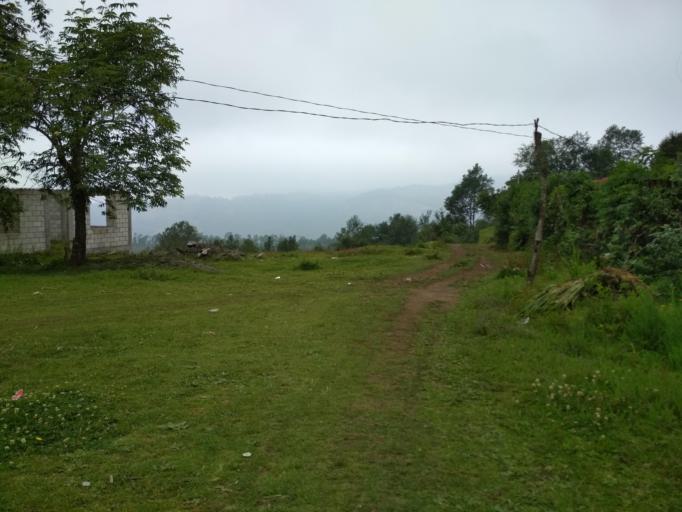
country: MX
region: Veracruz
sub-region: La Perla
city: Chilapa
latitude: 18.9995
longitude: -97.1658
